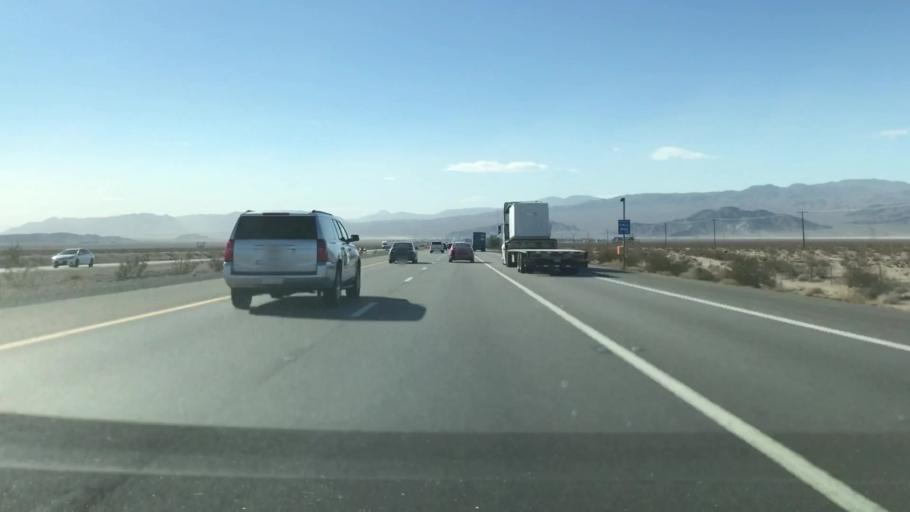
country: US
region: Nevada
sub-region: Clark County
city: Sandy Valley
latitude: 35.3033
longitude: -116.0158
